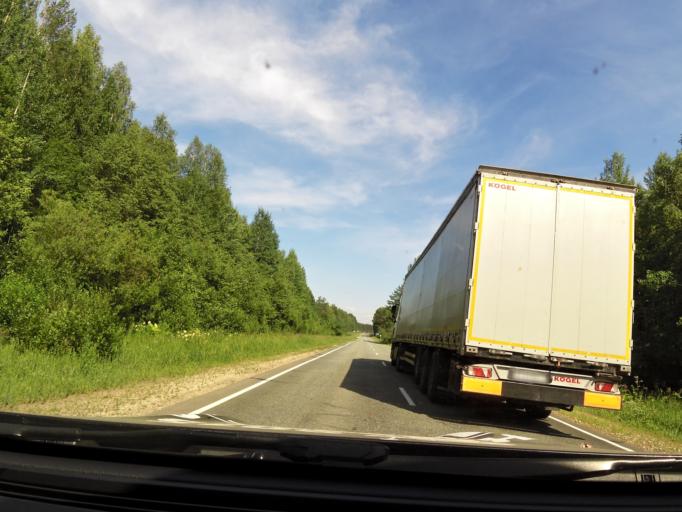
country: RU
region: Kirov
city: Belaya Kholunitsa
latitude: 58.8294
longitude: 50.6468
